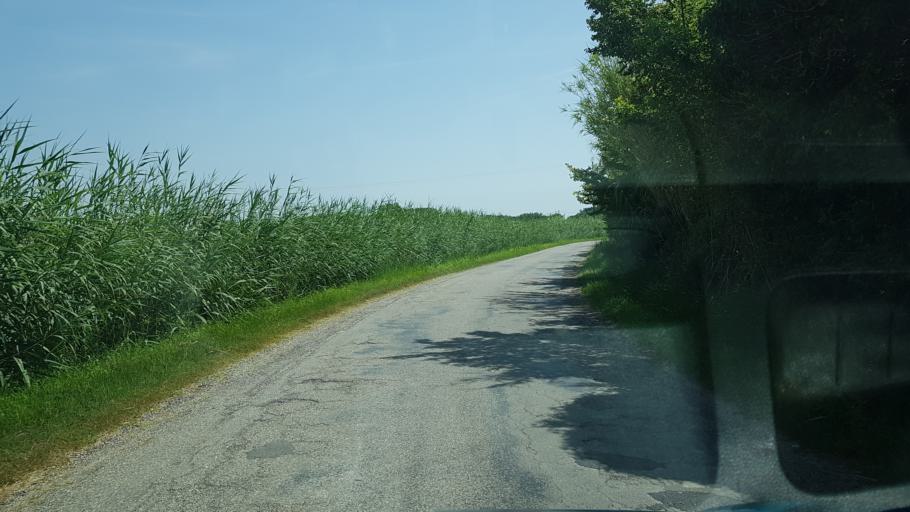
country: FR
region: Languedoc-Roussillon
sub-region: Departement du Gard
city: Fourques
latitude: 43.6344
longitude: 4.5693
